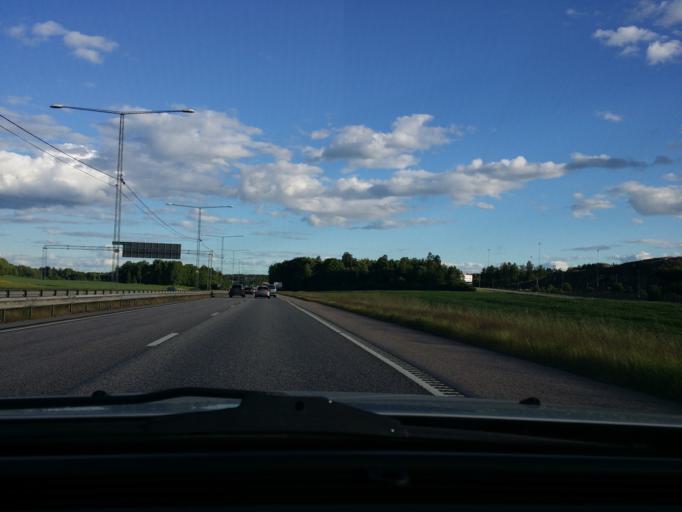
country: SE
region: Stockholm
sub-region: Sigtuna Kommun
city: Rosersberg
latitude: 59.5641
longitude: 17.8973
